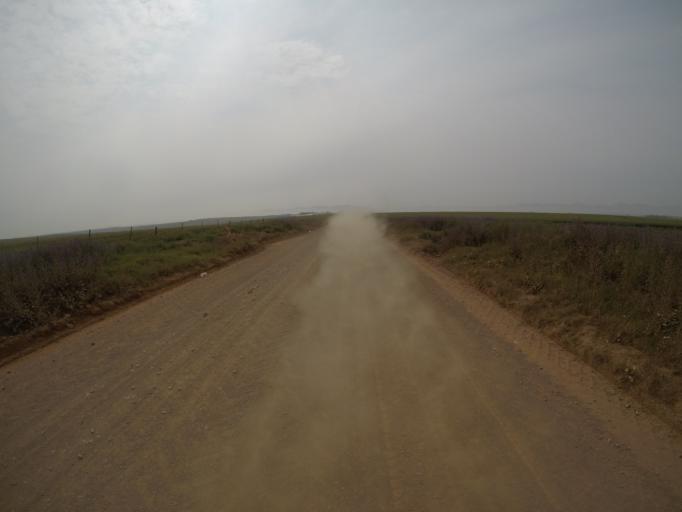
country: ZA
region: Western Cape
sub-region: City of Cape Town
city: Kraaifontein
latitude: -33.7175
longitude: 18.6803
